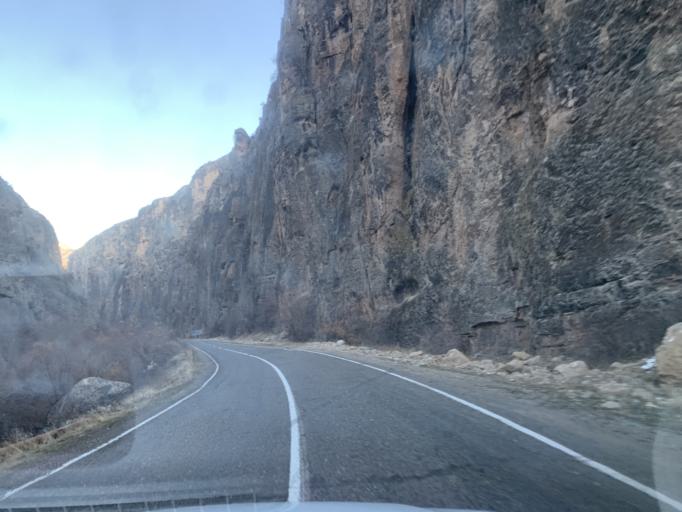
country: AM
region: Vayots' Dzori Marz
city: Areni
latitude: 39.7257
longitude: 45.2056
